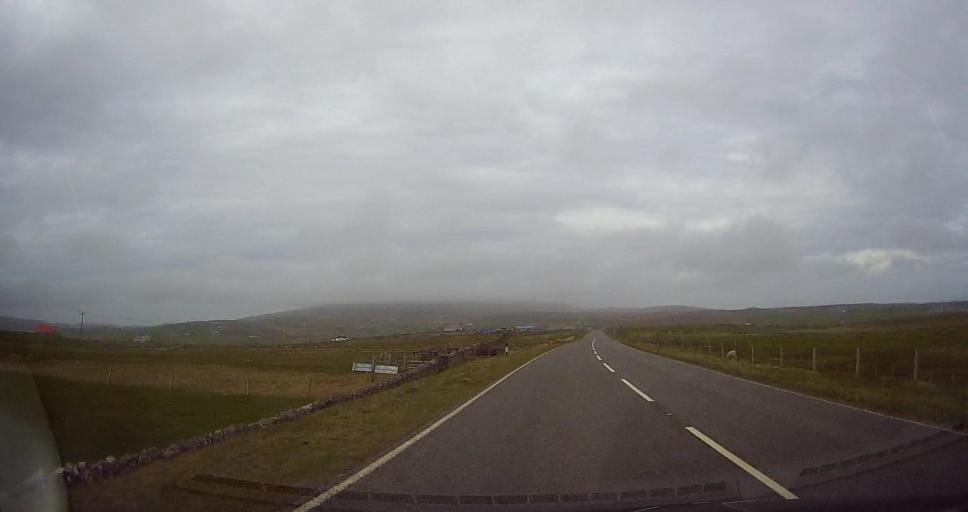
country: GB
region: Scotland
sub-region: Shetland Islands
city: Sandwick
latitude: 59.9134
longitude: -1.3019
